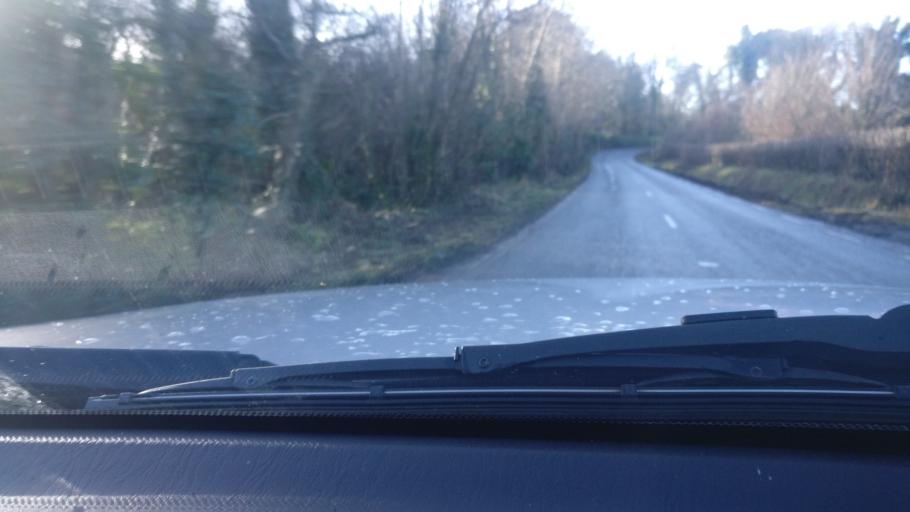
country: IE
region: Ulster
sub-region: An Cabhan
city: Ballyjamesduff
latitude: 53.8231
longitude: -7.3384
